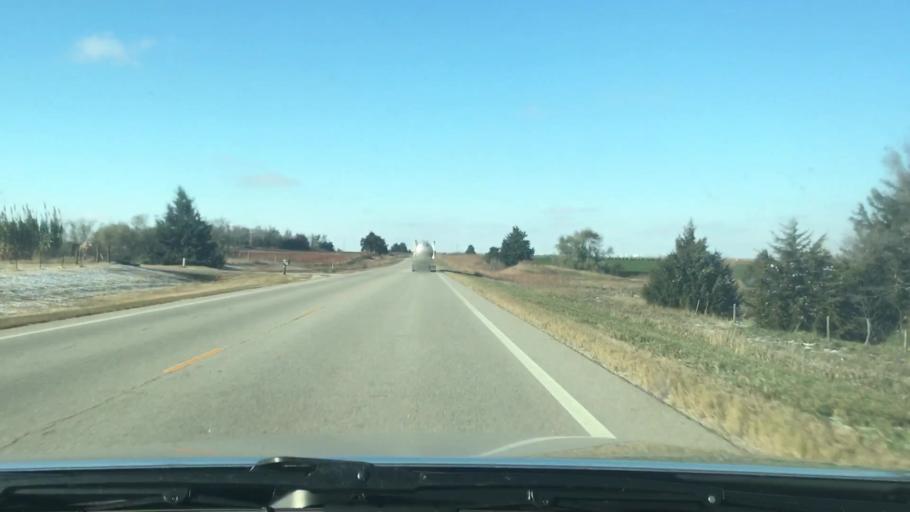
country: US
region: Kansas
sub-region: Rice County
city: Sterling
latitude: 38.1488
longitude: -98.2037
